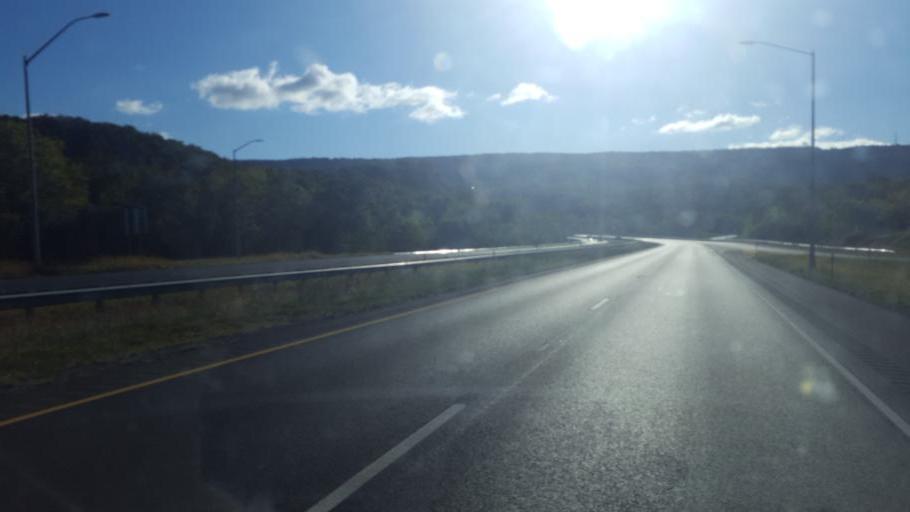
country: US
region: West Virginia
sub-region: Morgan County
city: Berkeley Springs
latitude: 39.7050
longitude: -78.3264
